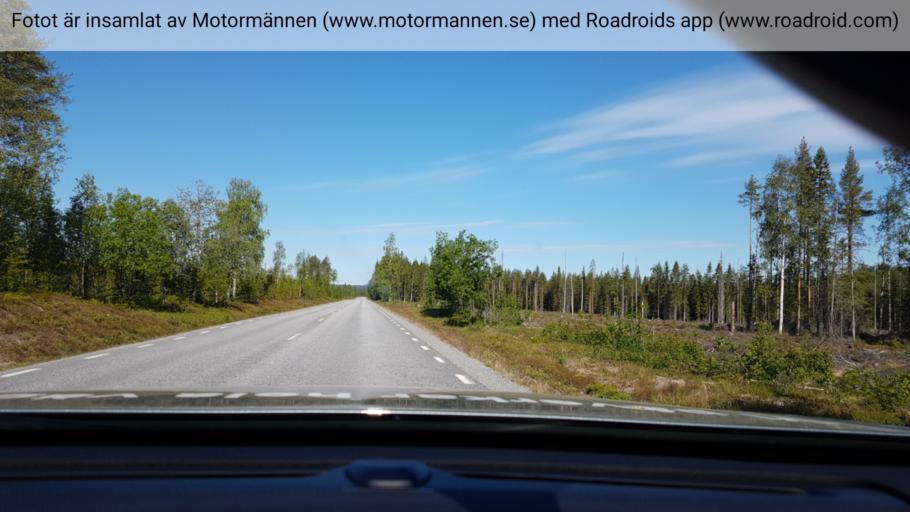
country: SE
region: Vaesterbotten
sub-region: Bjurholms Kommun
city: Bjurholm
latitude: 63.9555
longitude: 18.8777
